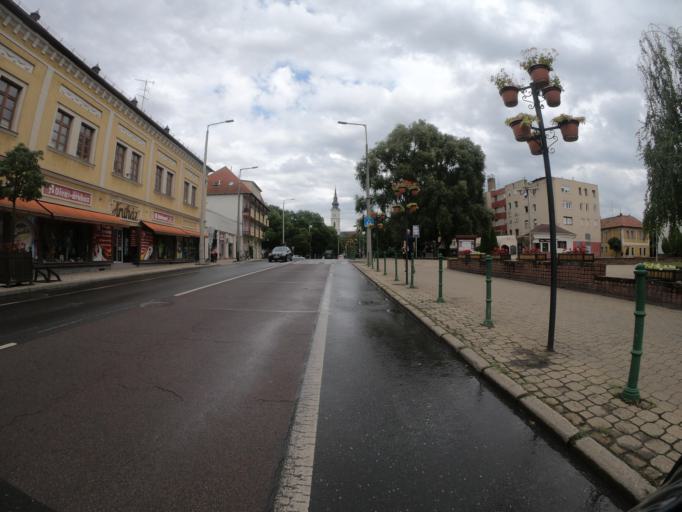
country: HU
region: Borsod-Abauj-Zemplen
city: Mezokovesd
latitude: 47.8105
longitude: 20.5718
